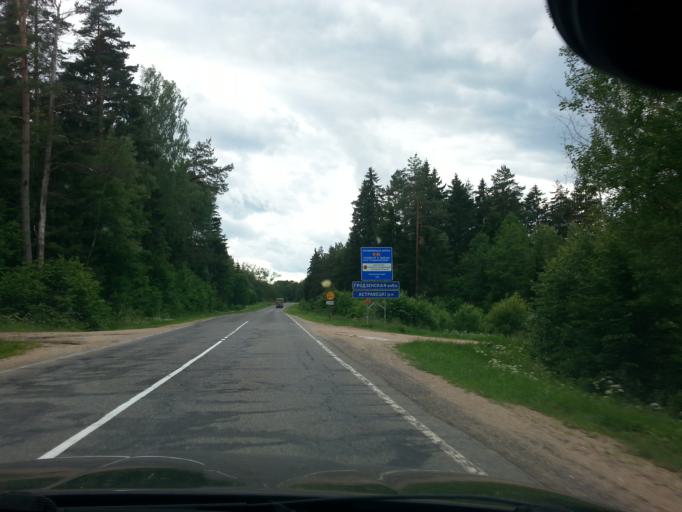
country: BY
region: Minsk
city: Svir
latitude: 54.8691
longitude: 26.3462
